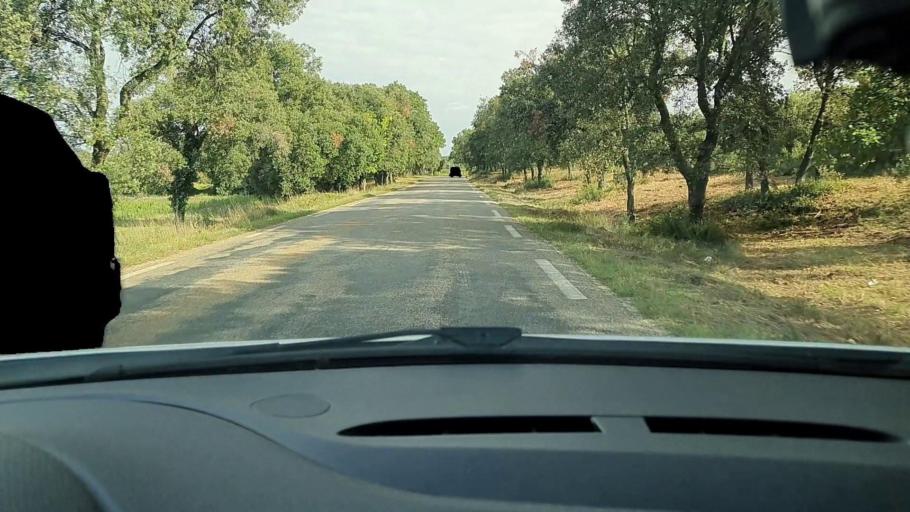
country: FR
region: Languedoc-Roussillon
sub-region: Departement du Gard
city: Saint-Quentin-la-Poterie
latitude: 44.0900
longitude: 4.4547
